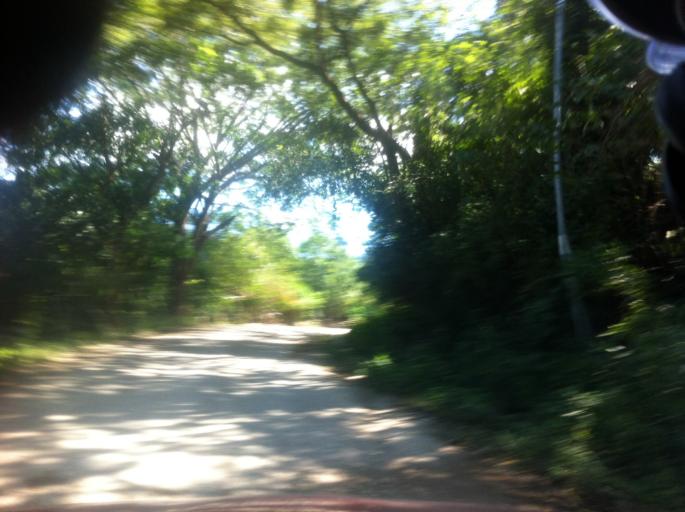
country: NI
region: Boaco
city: San Jose de los Remates
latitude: 12.6673
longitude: -85.7819
